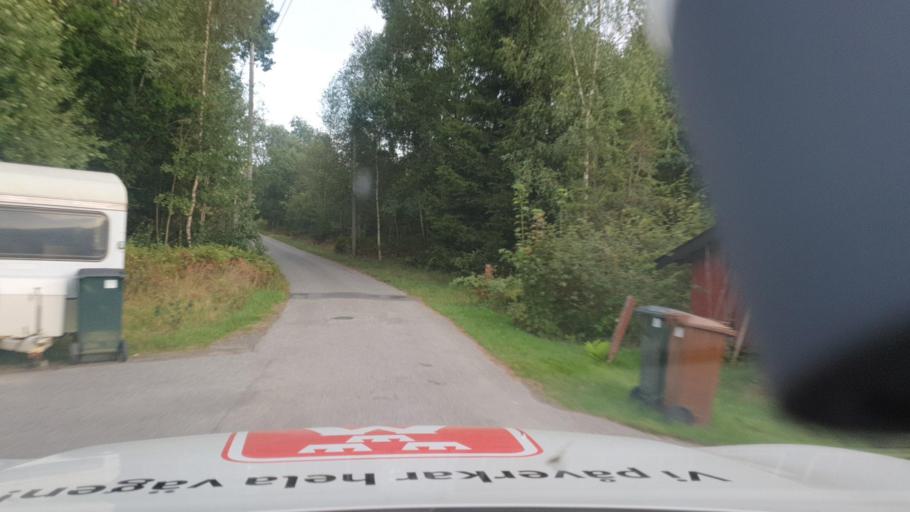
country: SE
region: Vaestra Goetaland
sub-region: Harryda Kommun
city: Hindas
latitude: 57.6985
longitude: 12.4640
